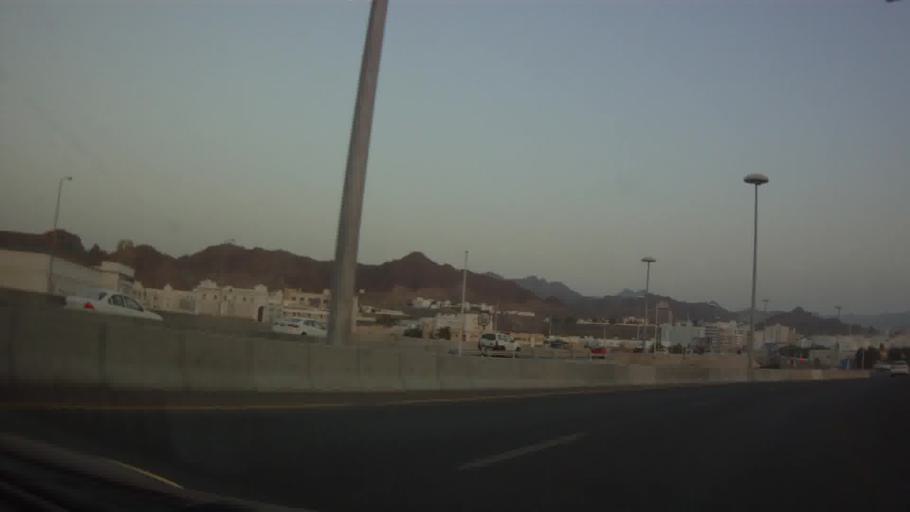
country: OM
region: Muhafazat Masqat
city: Muscat
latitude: 23.6177
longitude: 58.5434
